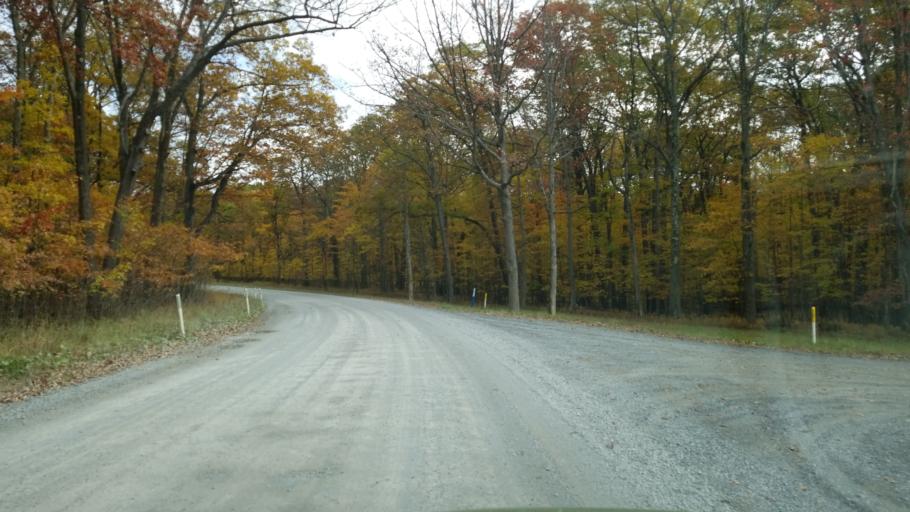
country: US
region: Pennsylvania
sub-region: Clearfield County
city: Clearfield
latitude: 41.1446
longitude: -78.4739
